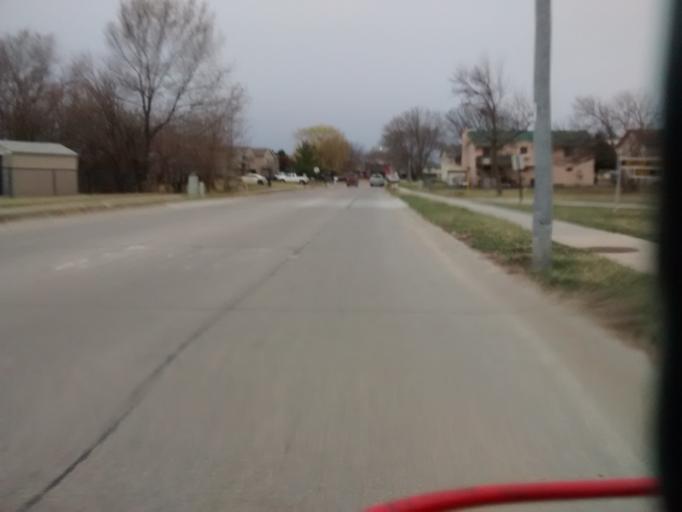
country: US
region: Nebraska
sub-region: Sarpy County
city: Offutt Air Force Base
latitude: 41.1490
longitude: -95.9419
